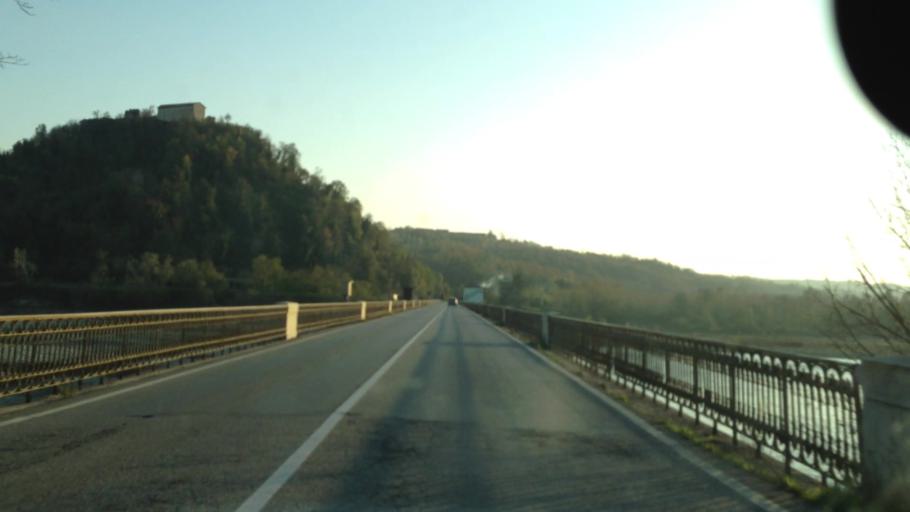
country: IT
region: Piedmont
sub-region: Provincia di Vercelli
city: Crescentino
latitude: 45.1797
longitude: 8.0997
